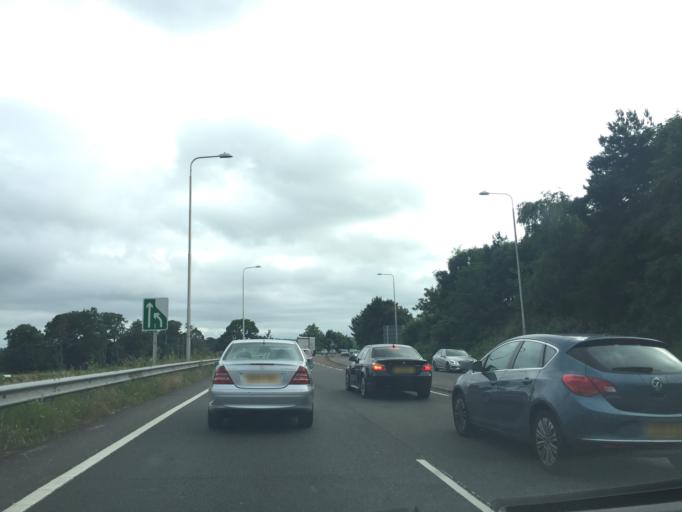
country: GB
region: England
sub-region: Dorset
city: Ferndown
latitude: 50.8014
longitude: -1.9398
